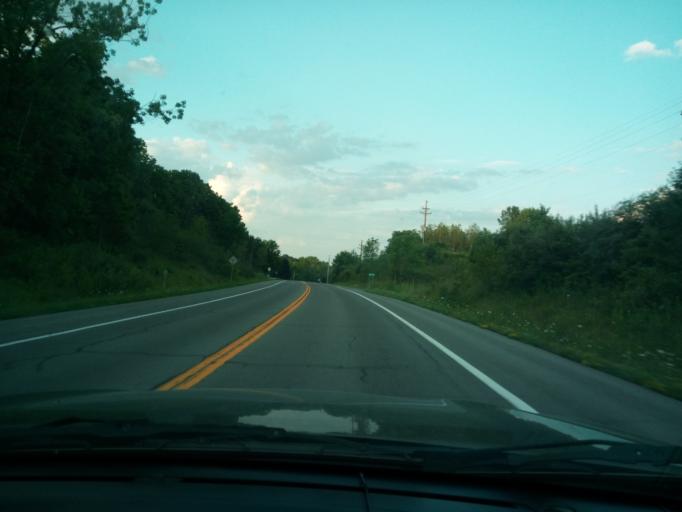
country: US
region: New York
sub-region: Wayne County
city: Clyde
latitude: 43.0684
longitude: -76.8015
